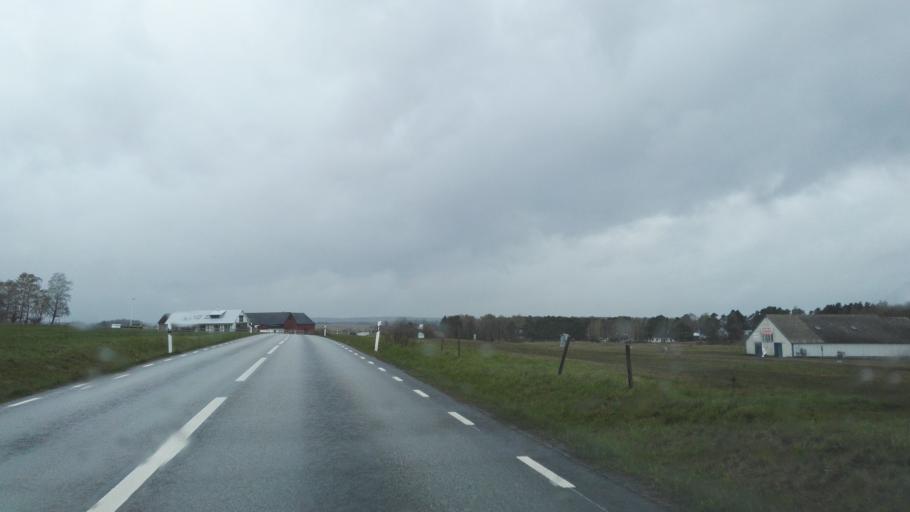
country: SE
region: Skane
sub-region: Simrishamns Kommun
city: Kivik
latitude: 55.6924
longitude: 14.2084
